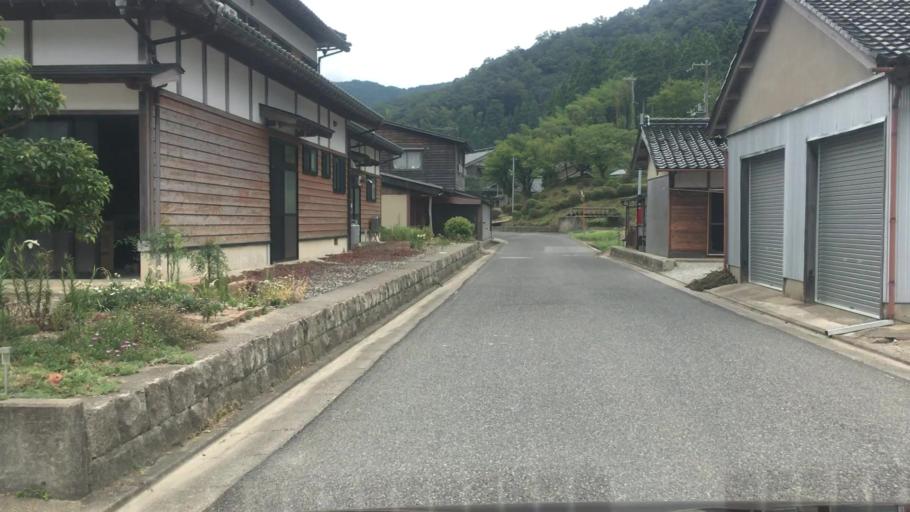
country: JP
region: Hyogo
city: Toyooka
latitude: 35.6338
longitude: 134.6804
